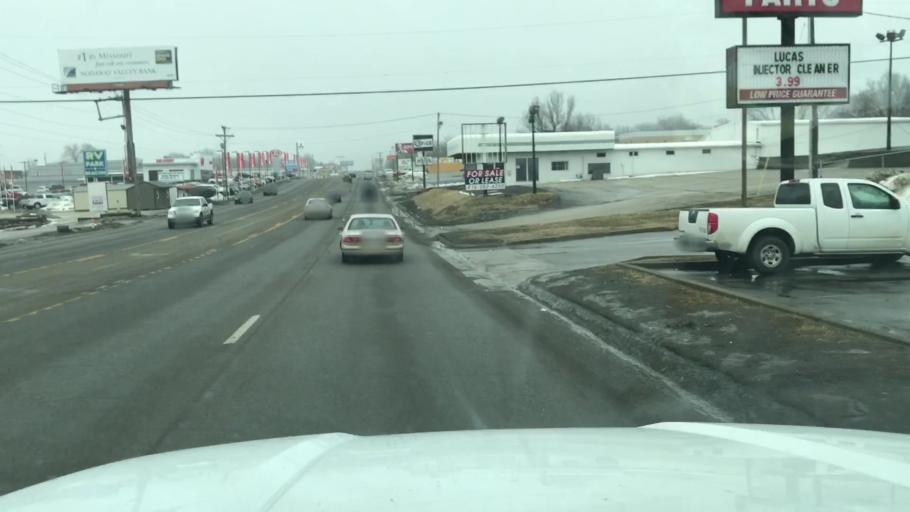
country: US
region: Missouri
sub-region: Buchanan County
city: Saint Joseph
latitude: 39.7576
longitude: -94.8037
